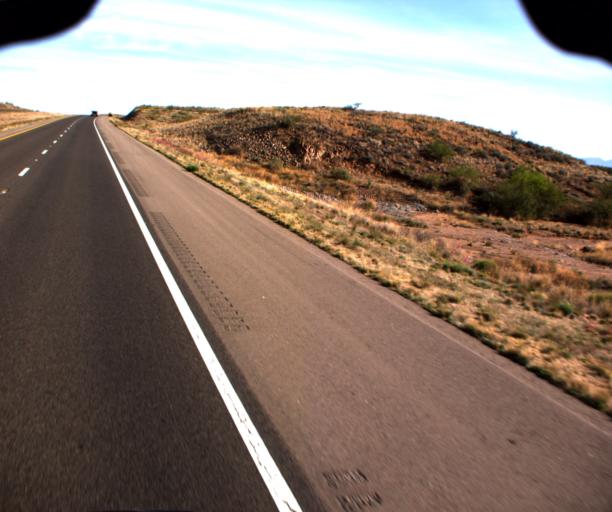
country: US
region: Arizona
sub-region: Cochise County
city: Willcox
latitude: 32.4380
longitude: -109.6635
